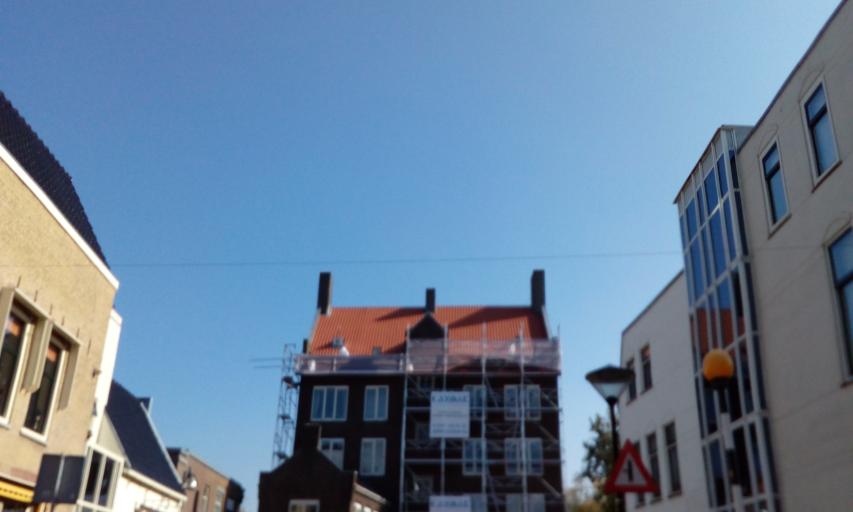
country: NL
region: South Holland
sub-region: Gemeente Vlaardingen
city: Vlaardingen
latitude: 51.9105
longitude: 4.3436
